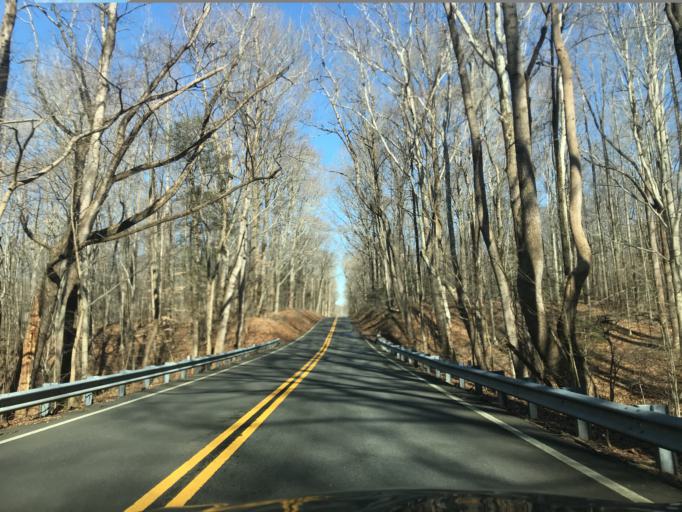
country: US
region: Virginia
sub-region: Prince William County
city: Quantico Station
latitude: 38.4969
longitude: -77.2526
